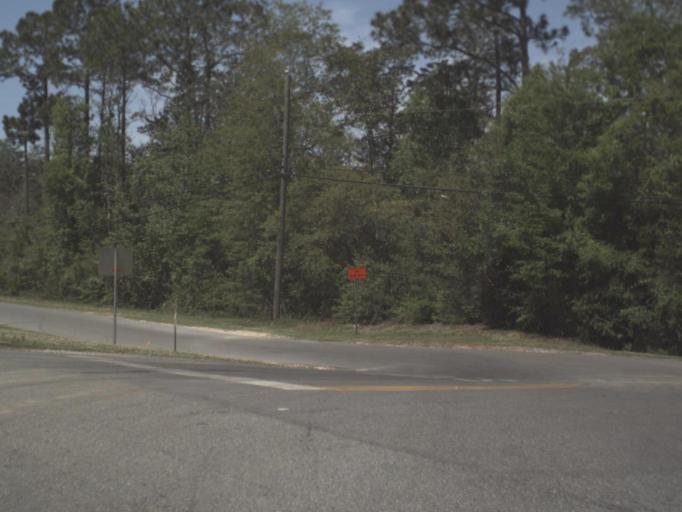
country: US
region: Florida
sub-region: Santa Rosa County
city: Milton
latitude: 30.6257
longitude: -87.0326
